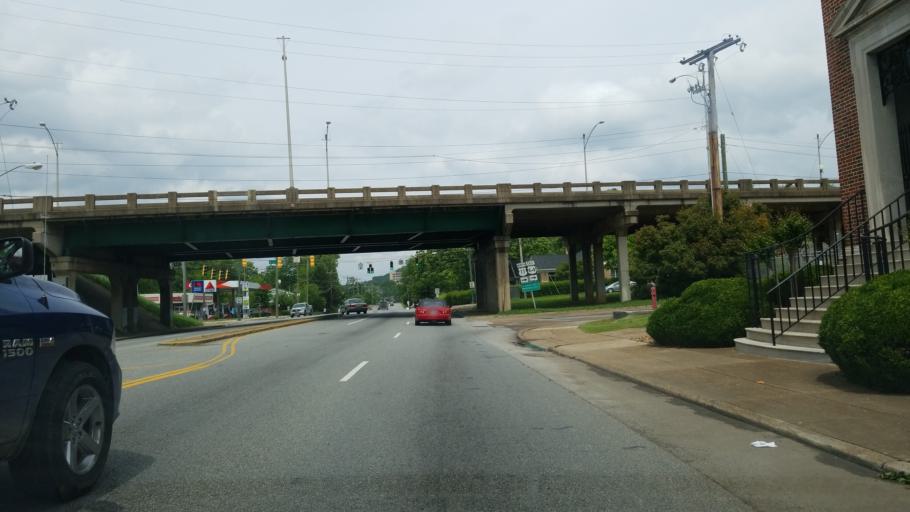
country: US
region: Tennessee
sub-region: Hamilton County
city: East Ridge
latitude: 35.0312
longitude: -85.2642
